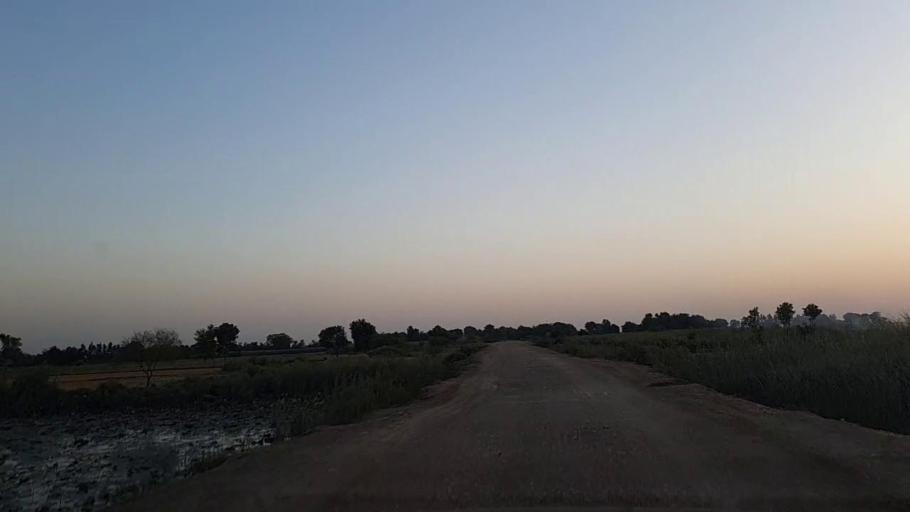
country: PK
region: Sindh
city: Mirpur Batoro
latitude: 24.6211
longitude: 68.1841
